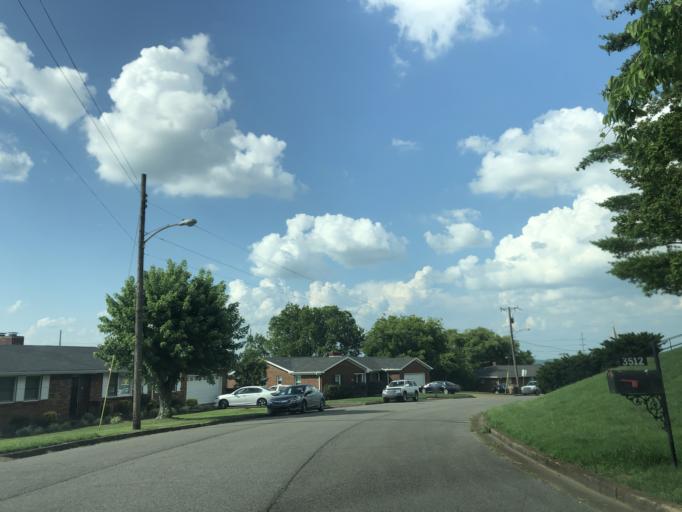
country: US
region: Tennessee
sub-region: Davidson County
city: Nashville
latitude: 36.1615
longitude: -86.8294
